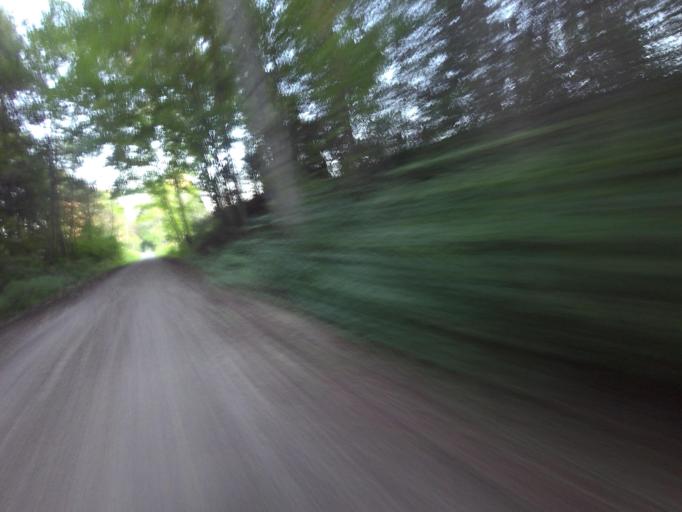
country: CA
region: Ontario
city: Goderich
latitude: 43.7517
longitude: -81.6228
